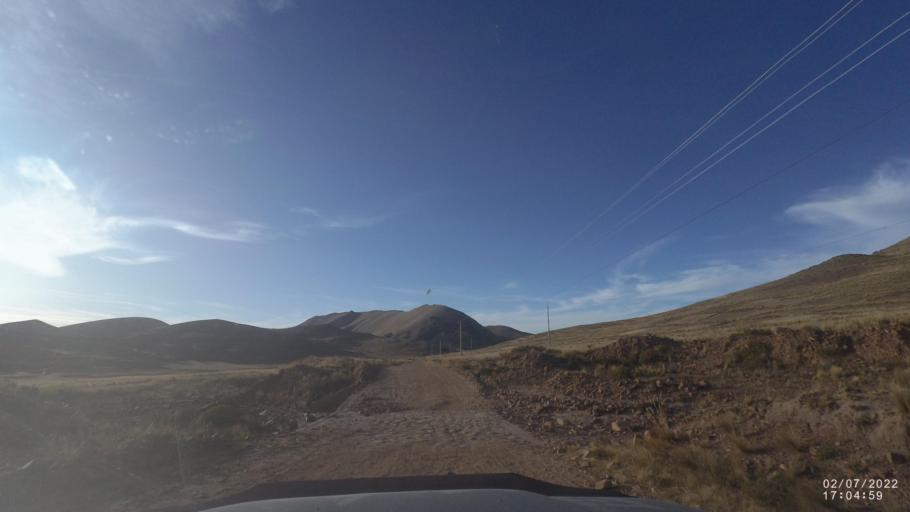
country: BO
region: Cochabamba
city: Irpa Irpa
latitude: -17.9104
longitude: -66.5597
